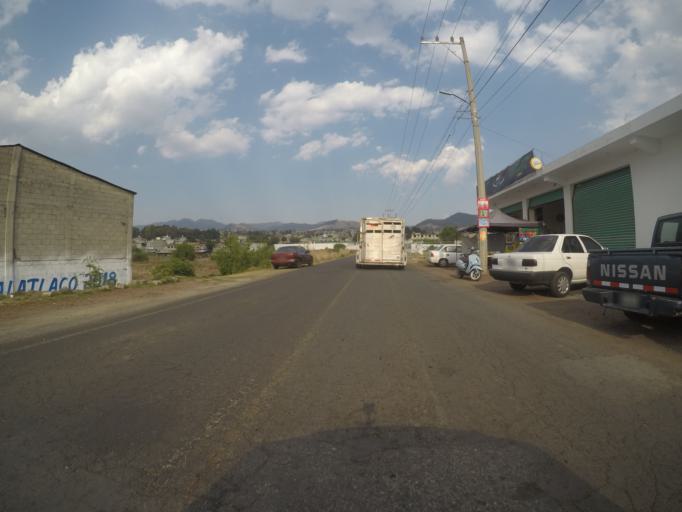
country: MX
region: Mexico
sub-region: Xalatlaco
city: Techichili
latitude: 19.1718
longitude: -99.4140
